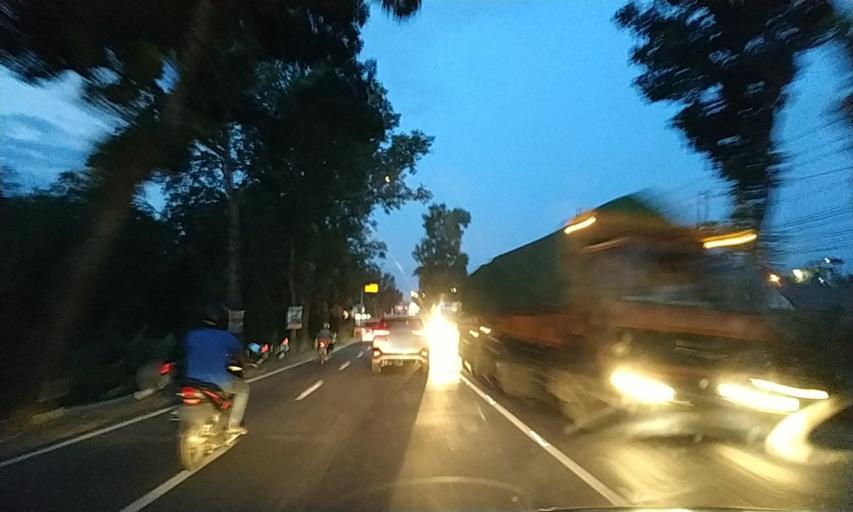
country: ID
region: Daerah Istimewa Yogyakarta
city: Godean
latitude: -7.8137
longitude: 110.2603
